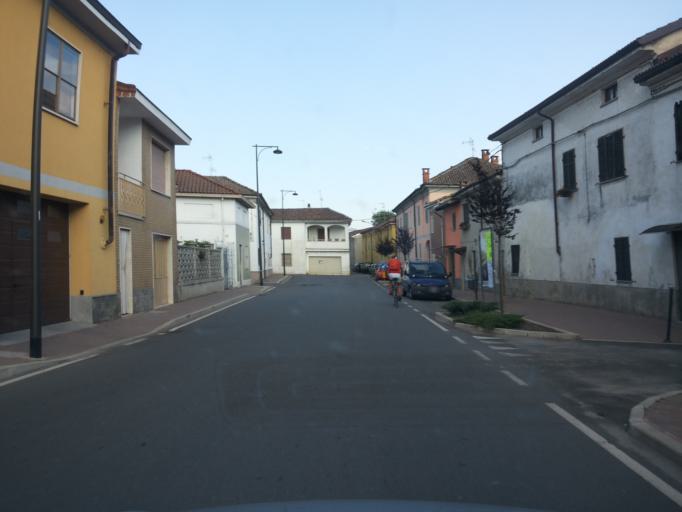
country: IT
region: Piedmont
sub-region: Provincia di Vercelli
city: Asigliano Vercellese
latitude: 45.2619
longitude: 8.4086
